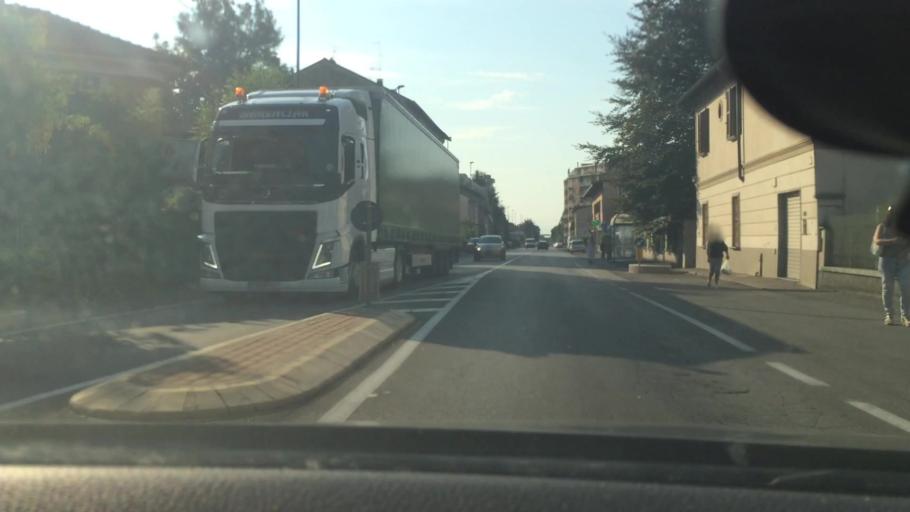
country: IT
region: Lombardy
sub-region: Provincia di Varese
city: Gerenzano
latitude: 45.6418
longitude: 9.0023
